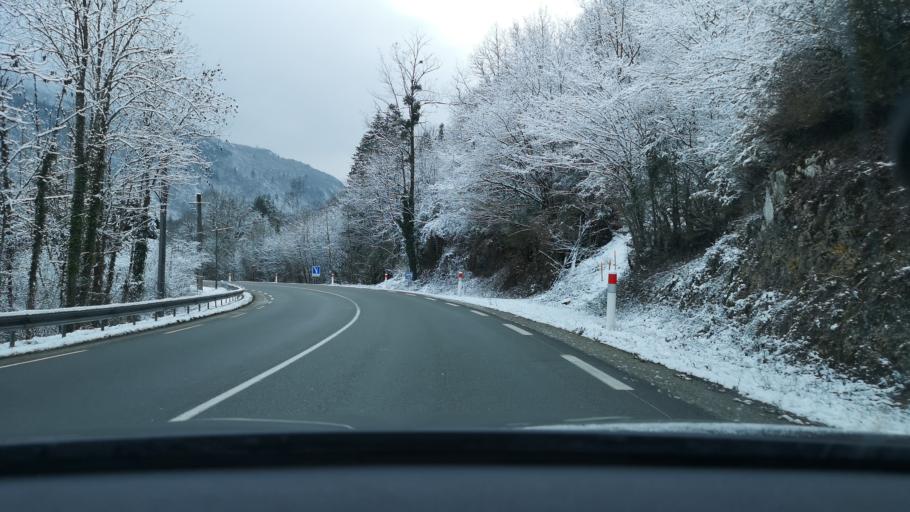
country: FR
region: Rhone-Alpes
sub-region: Departement de l'Ain
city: Dortan
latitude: 46.3699
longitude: 5.7042
